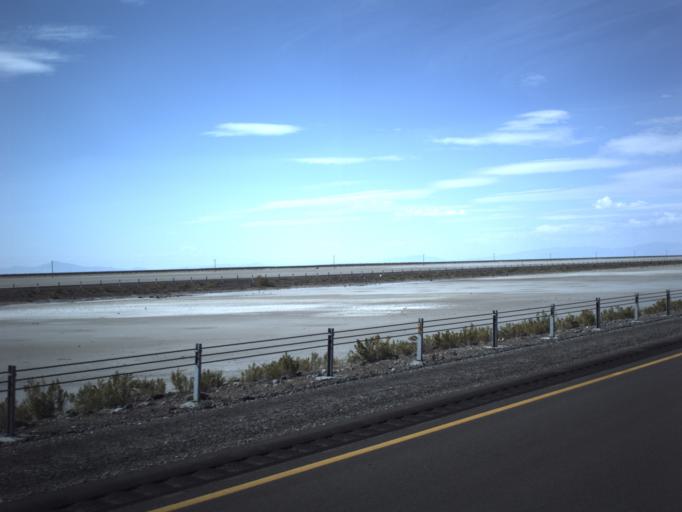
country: US
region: Utah
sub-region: Tooele County
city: Wendover
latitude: 40.7289
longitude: -113.3691
